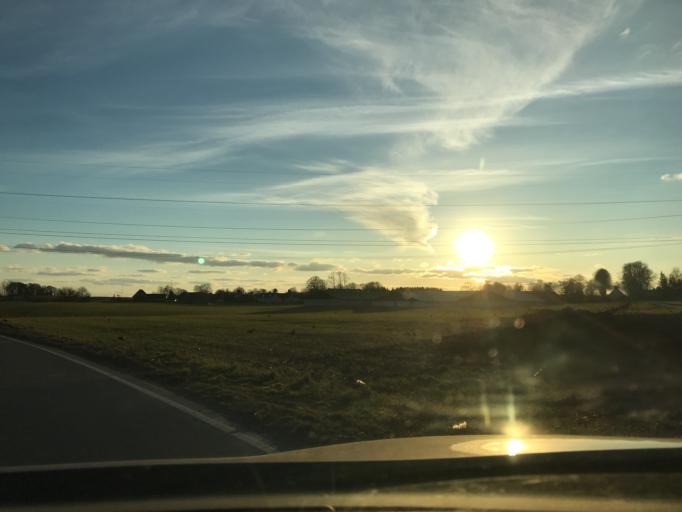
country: DK
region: South Denmark
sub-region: Middelfart Kommune
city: Norre Aby
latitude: 55.4580
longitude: 9.8473
